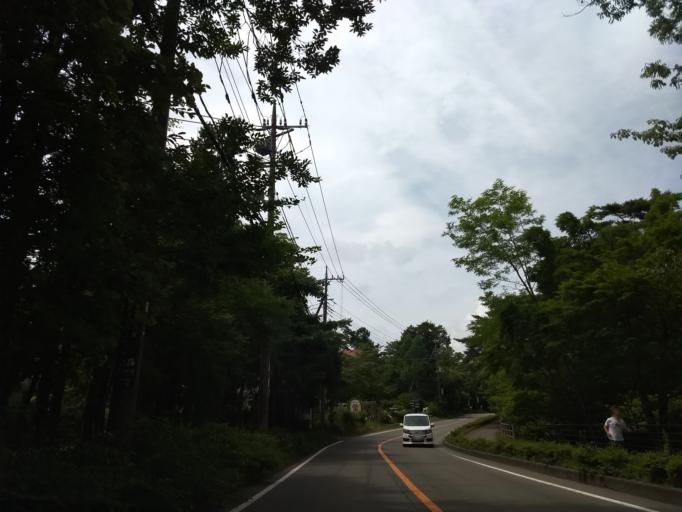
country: JP
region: Shizuoka
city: Gotemba
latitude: 35.4099
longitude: 138.8867
